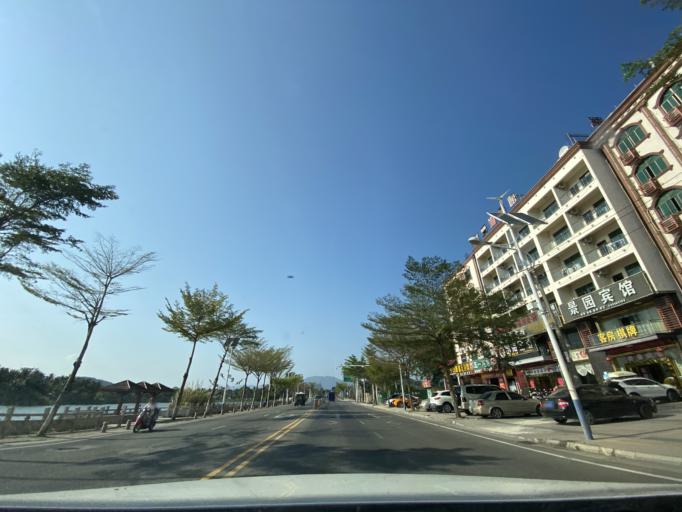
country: CN
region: Hainan
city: Yingzhou
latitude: 18.4318
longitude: 109.8529
